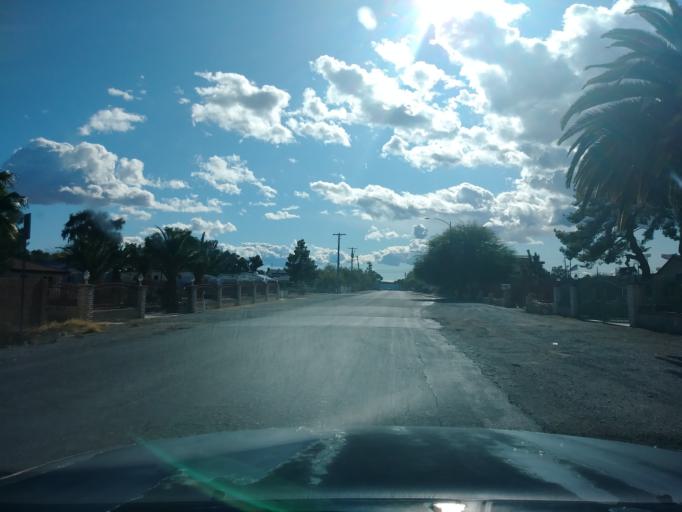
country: US
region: Nevada
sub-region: Clark County
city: Spring Valley
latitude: 36.1478
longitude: -115.2233
